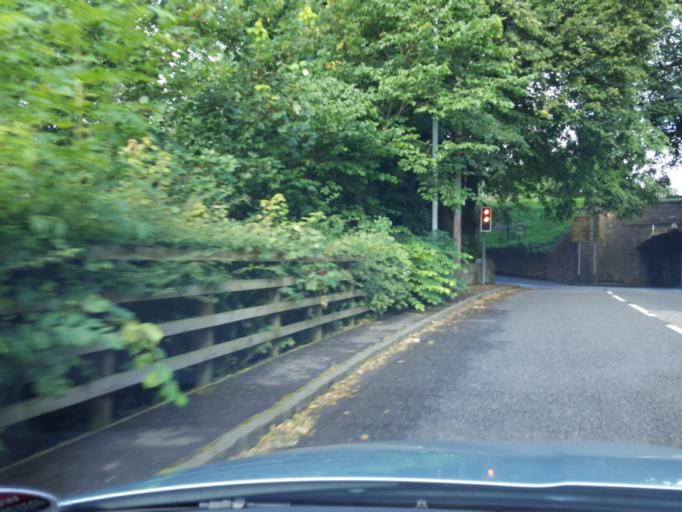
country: GB
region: Scotland
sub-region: West Lothian
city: Linlithgow
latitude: 55.9755
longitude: -3.5839
